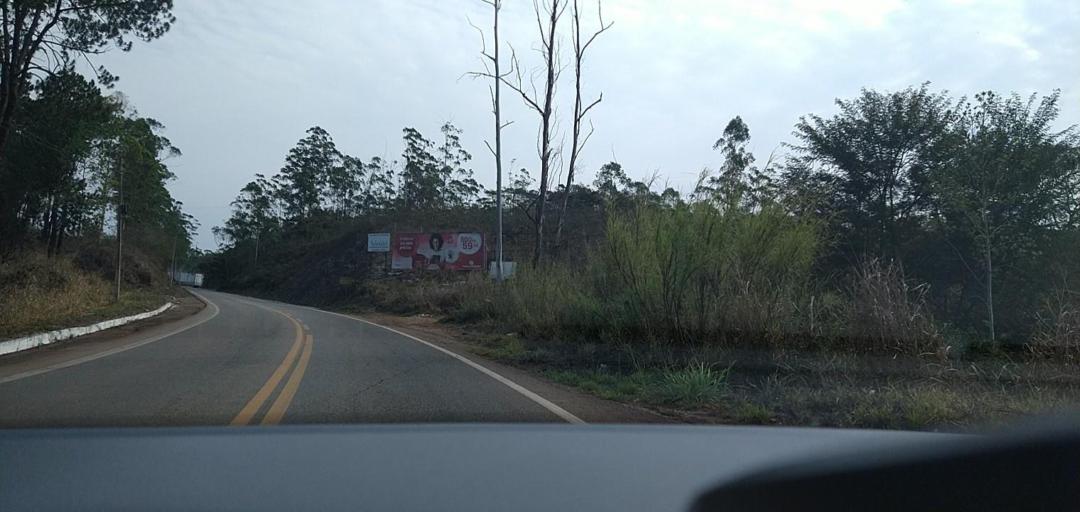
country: BR
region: Minas Gerais
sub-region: Rio Piracicaba
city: Rio Piracicaba
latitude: -19.8806
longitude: -43.1288
